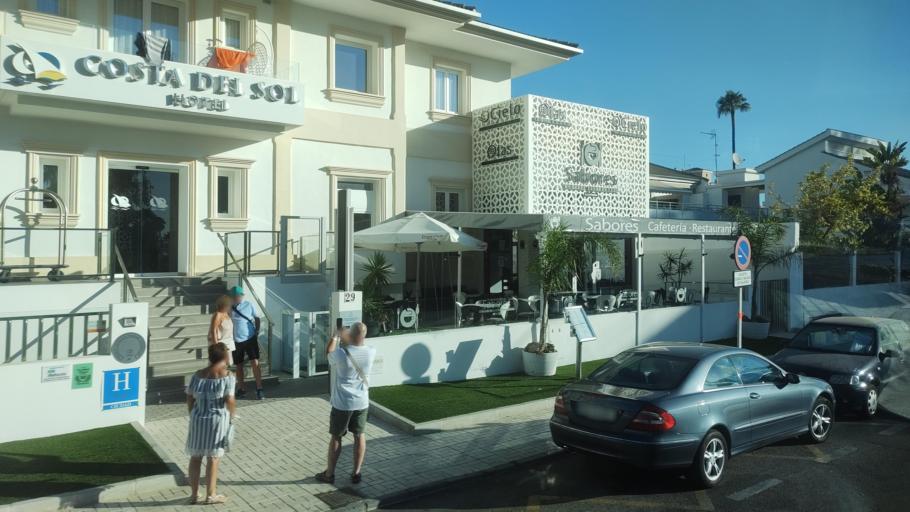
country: ES
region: Andalusia
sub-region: Provincia de Malaga
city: Torremolinos
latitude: 36.6321
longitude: -4.4924
